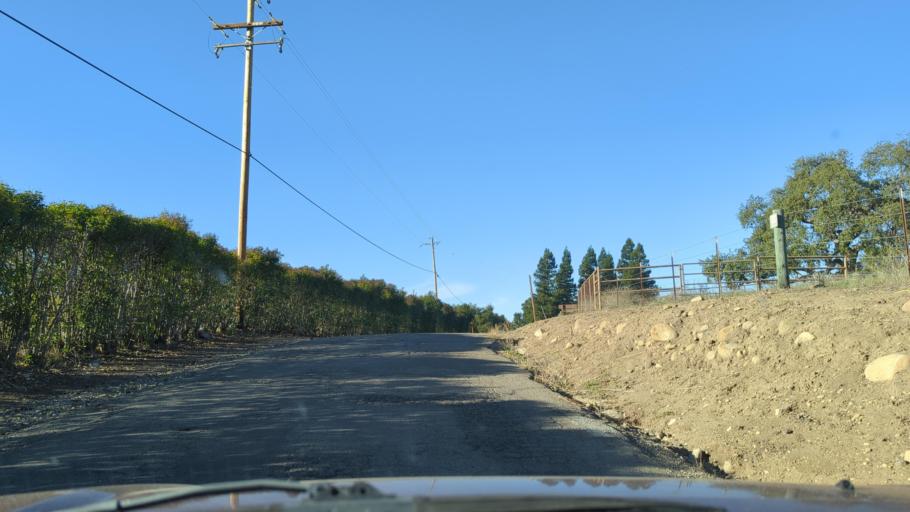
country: US
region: California
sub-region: Santa Barbara County
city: Santa Ynez
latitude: 34.5736
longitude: -120.0975
